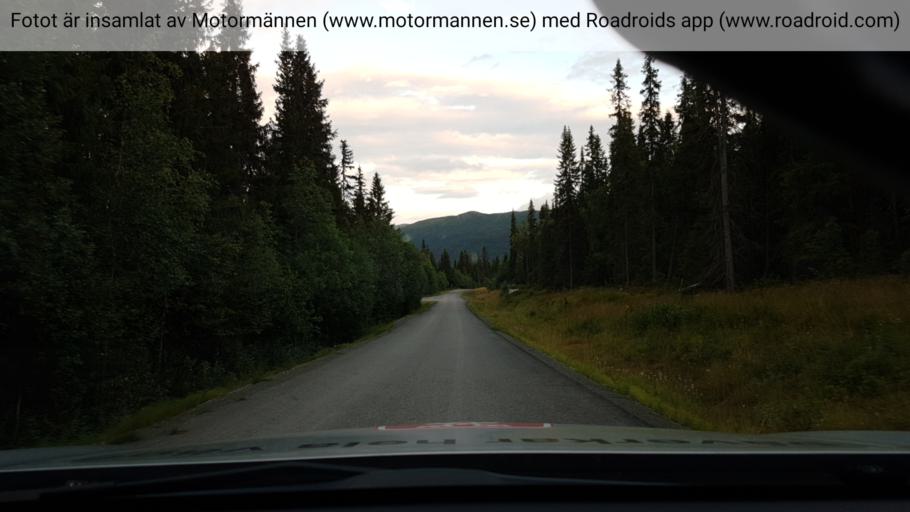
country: SE
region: Vaesterbotten
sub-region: Vilhelmina Kommun
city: Sjoberg
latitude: 65.5044
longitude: 15.6215
